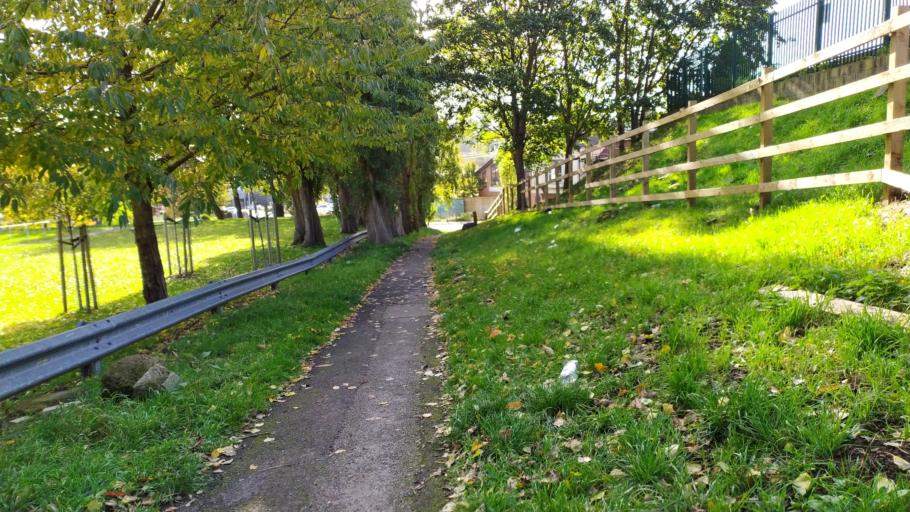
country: GB
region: England
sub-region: City and Borough of Leeds
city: Chapel Allerton
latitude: 53.8137
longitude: -1.5372
